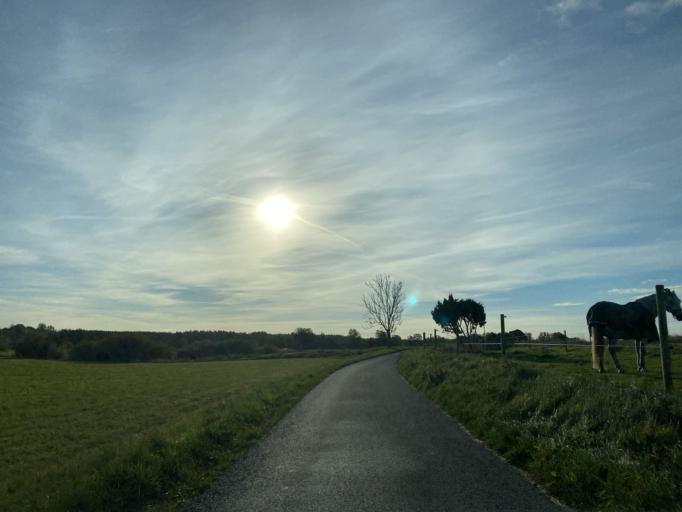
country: DK
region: Capital Region
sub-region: Allerod Kommune
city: Lynge
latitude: 55.8149
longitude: 12.2858
